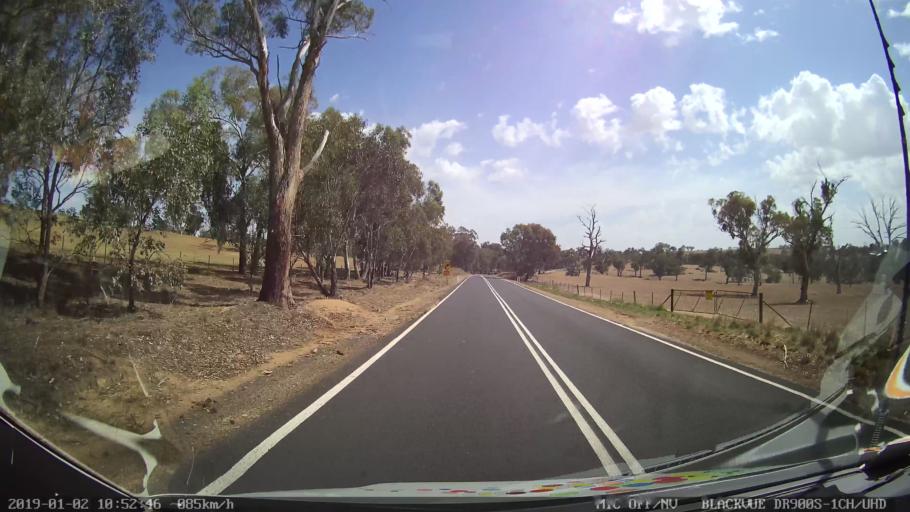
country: AU
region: New South Wales
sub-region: Cootamundra
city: Cootamundra
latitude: -34.6851
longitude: 148.2714
